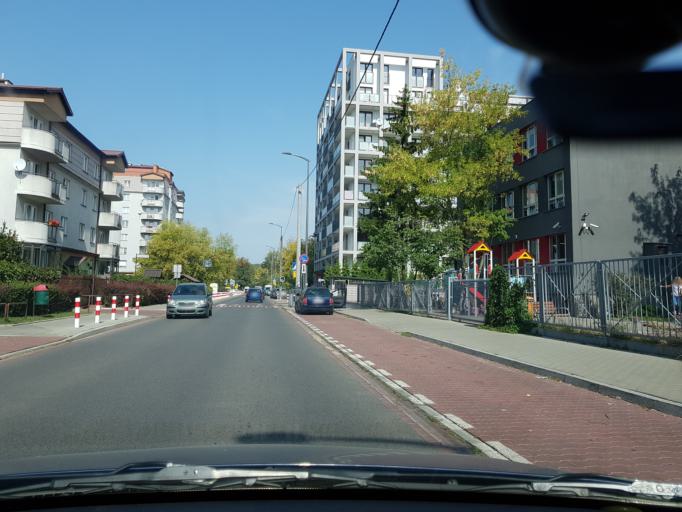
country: PL
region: Masovian Voivodeship
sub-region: Warszawa
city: Bielany
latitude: 52.2757
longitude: 20.9302
